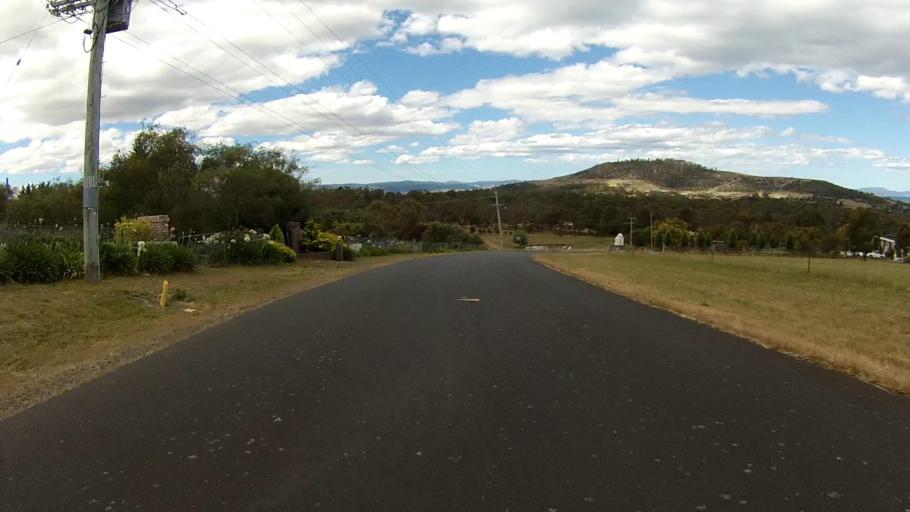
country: AU
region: Tasmania
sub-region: Clarence
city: Acton Park
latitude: -42.8815
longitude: 147.4708
